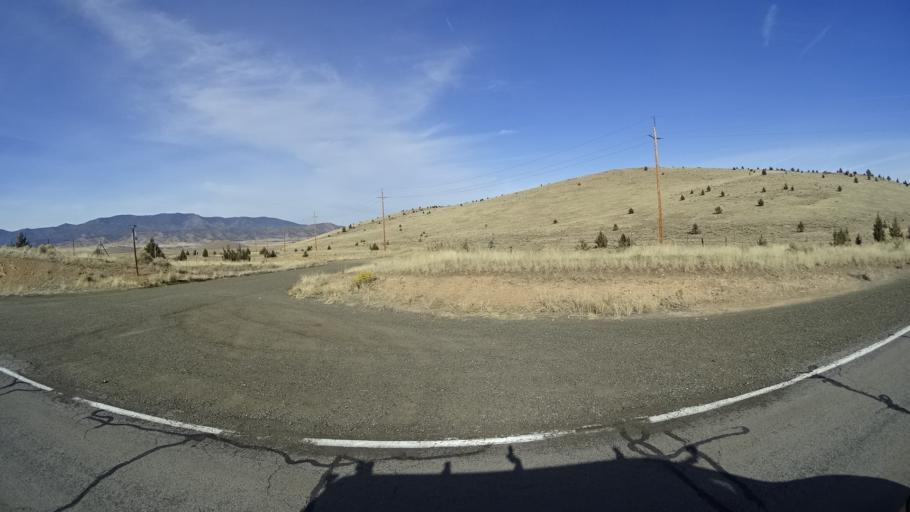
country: US
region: California
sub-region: Siskiyou County
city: Weed
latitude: 41.5535
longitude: -122.4823
